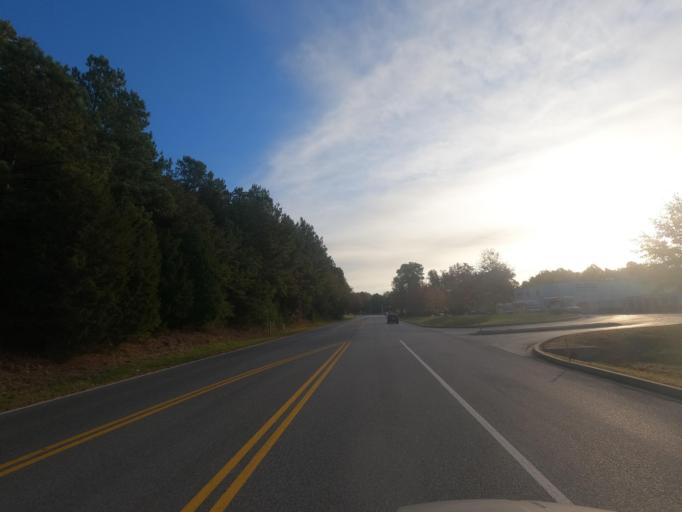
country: US
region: Maryland
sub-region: Calvert County
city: Lusby
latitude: 38.3887
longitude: -76.4343
